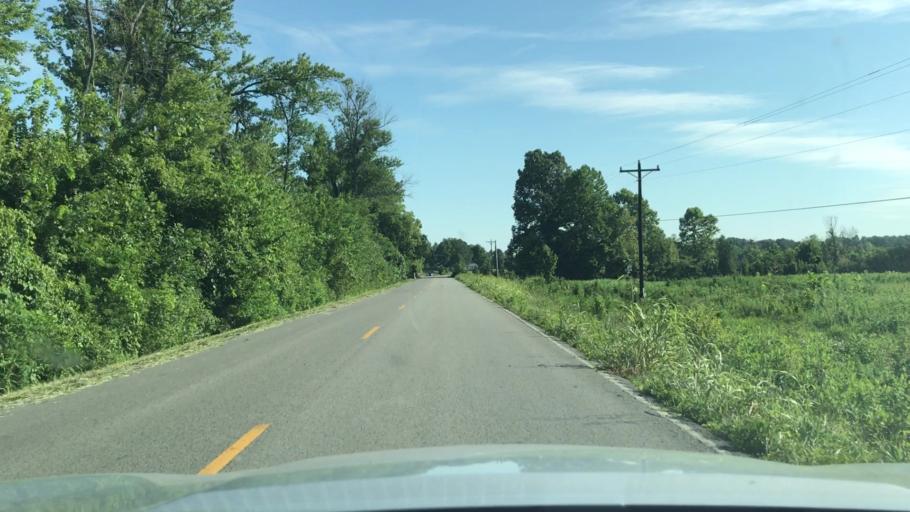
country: US
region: Kentucky
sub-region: Muhlenberg County
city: Greenville
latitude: 37.1422
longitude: -87.1422
